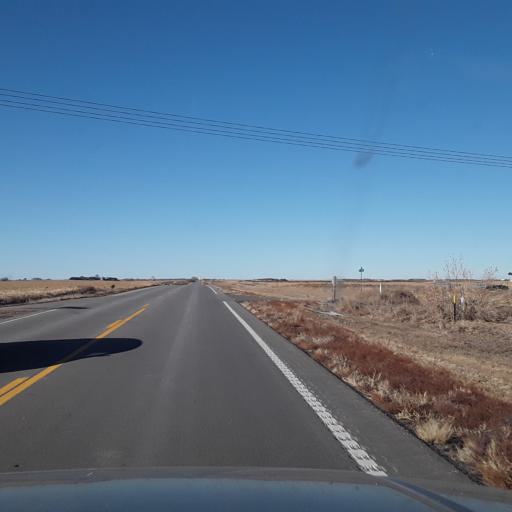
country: US
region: Nebraska
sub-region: Phelps County
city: Holdrege
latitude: 40.4878
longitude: -99.5300
